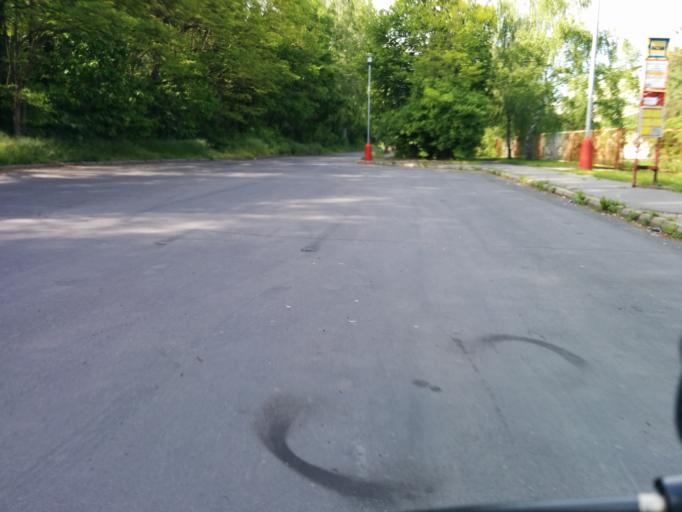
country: CZ
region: Central Bohemia
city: Neratovice
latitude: 50.2703
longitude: 14.5139
